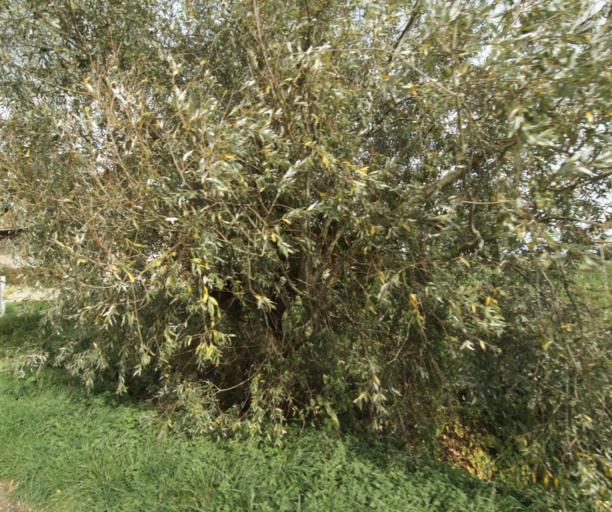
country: FR
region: Nord-Pas-de-Calais
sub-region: Departement du Pas-de-Calais
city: Fleurbaix
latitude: 50.6563
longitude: 2.8488
